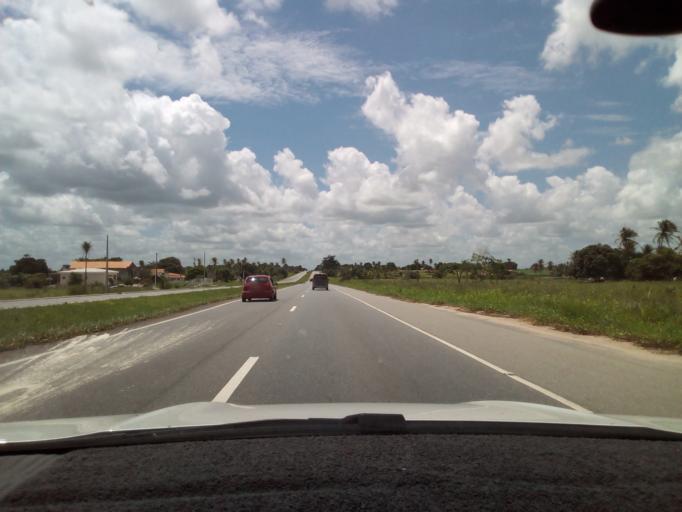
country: BR
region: Paraiba
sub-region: Pilar
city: Pilar
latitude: -7.1825
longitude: -35.3060
